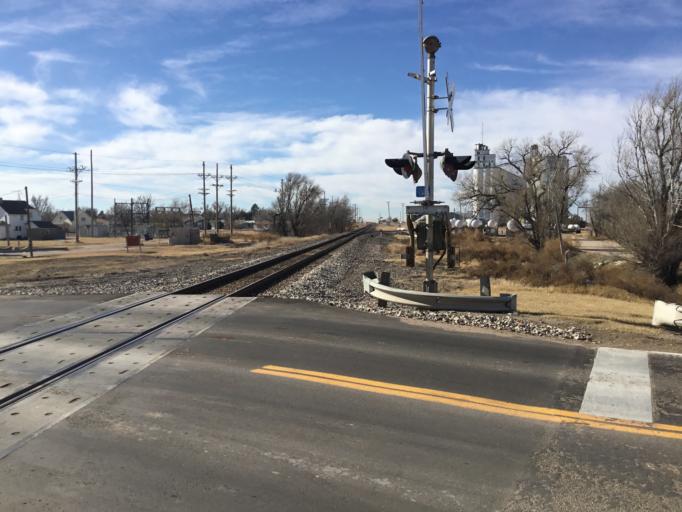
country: US
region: Kansas
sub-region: Ford County
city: Dodge City
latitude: 37.4447
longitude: -100.0153
